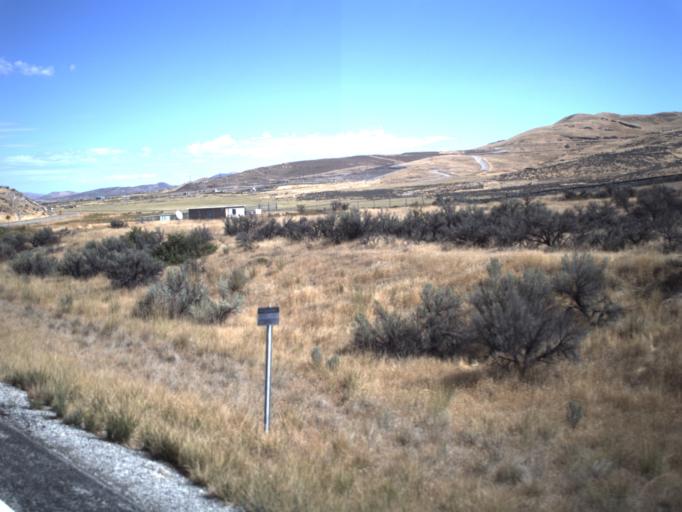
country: US
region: Utah
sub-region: Box Elder County
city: Tremonton
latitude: 41.6719
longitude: -112.4473
